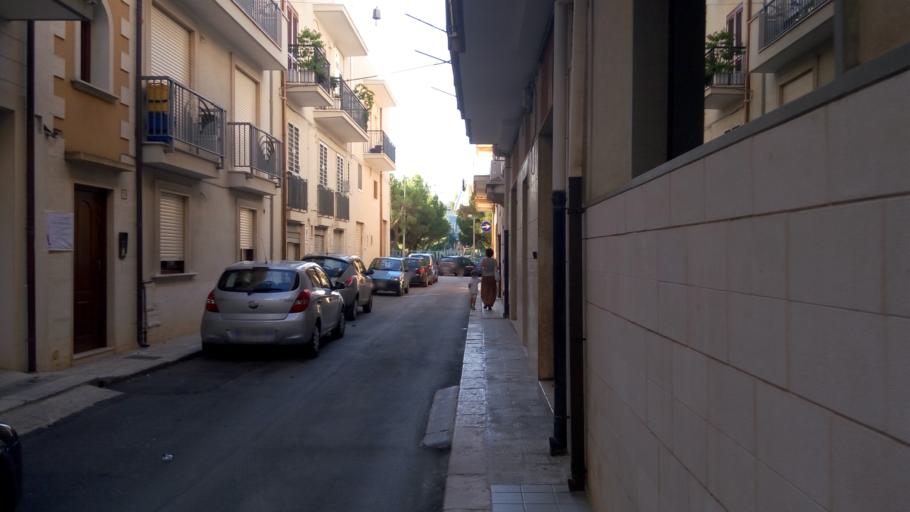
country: IT
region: Apulia
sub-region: Provincia di Bari
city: Polignano a Mare
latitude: 40.9917
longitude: 17.2223
